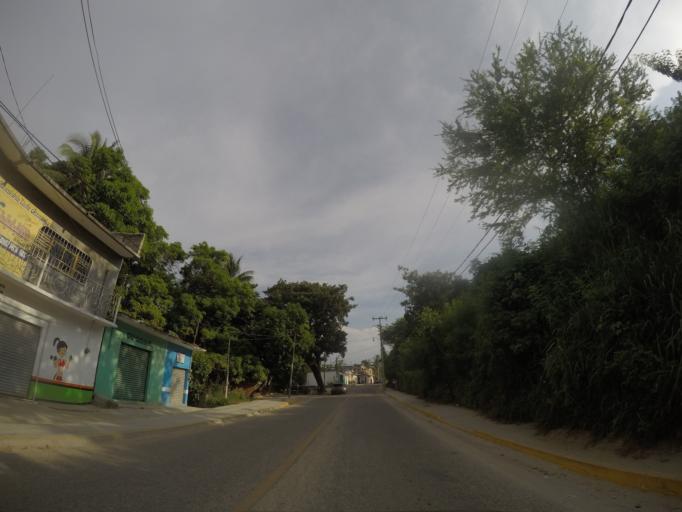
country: MX
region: Oaxaca
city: San Pedro Pochutla
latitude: 15.7535
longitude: -96.4648
